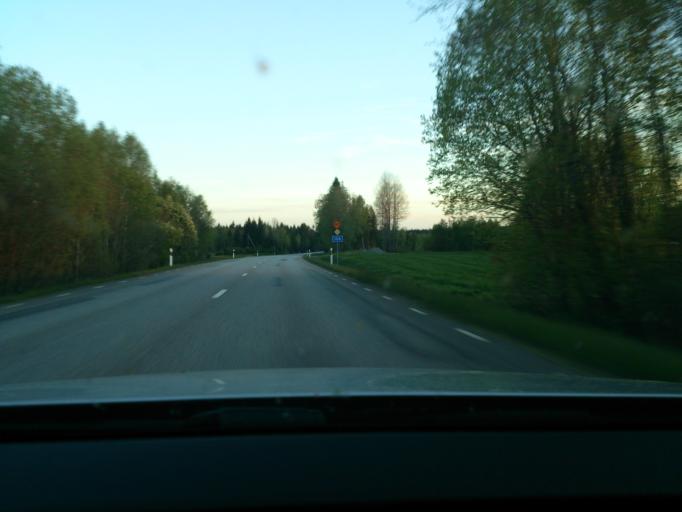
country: SE
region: Kronoberg
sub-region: Alvesta Kommun
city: Moheda
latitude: 57.0646
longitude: 14.6039
